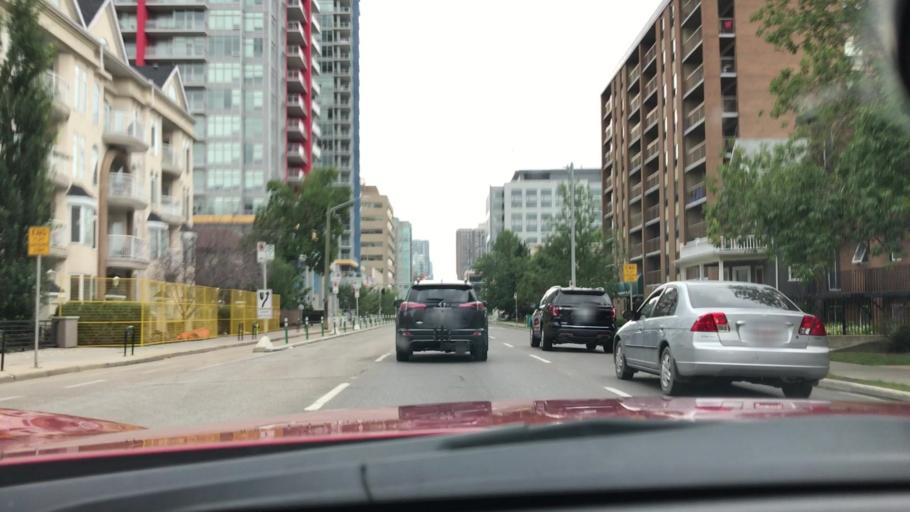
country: CA
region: Alberta
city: Calgary
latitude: 51.0421
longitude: -114.0860
